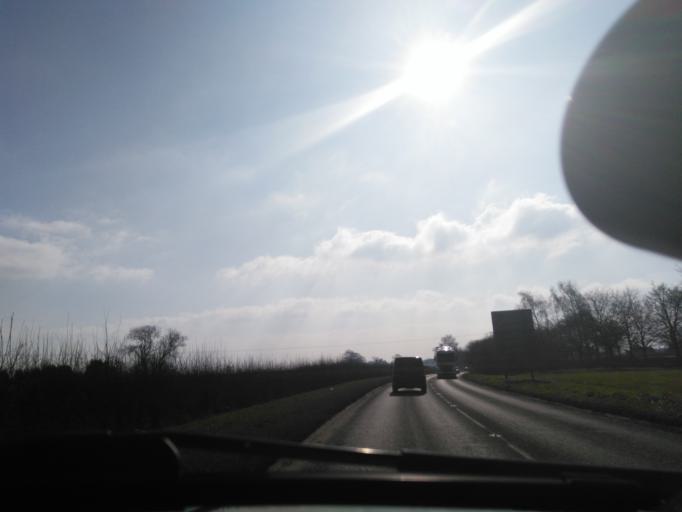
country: GB
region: England
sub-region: Wiltshire
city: Malmesbury
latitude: 51.5893
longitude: -2.0884
